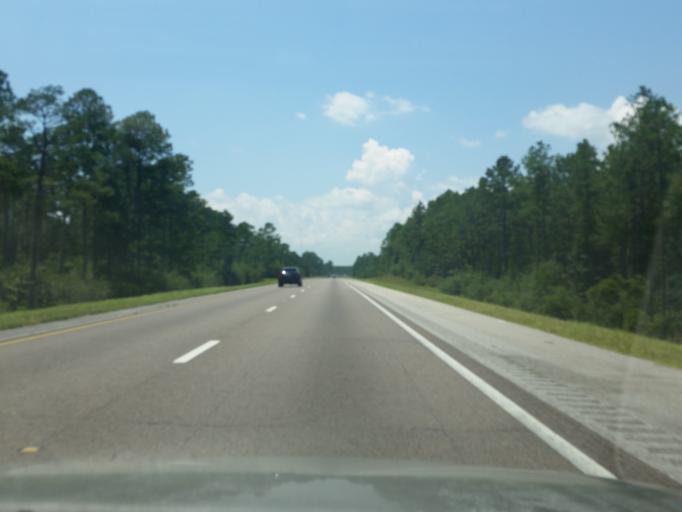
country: US
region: Alabama
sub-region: Baldwin County
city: Elberta
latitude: 30.5851
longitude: -87.5264
